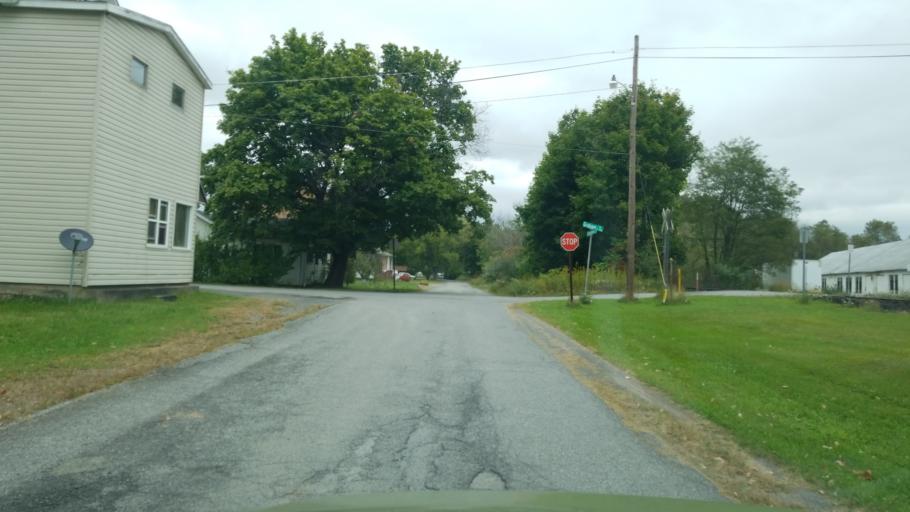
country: US
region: Pennsylvania
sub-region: Clearfield County
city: Hyde
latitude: 41.0006
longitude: -78.4628
